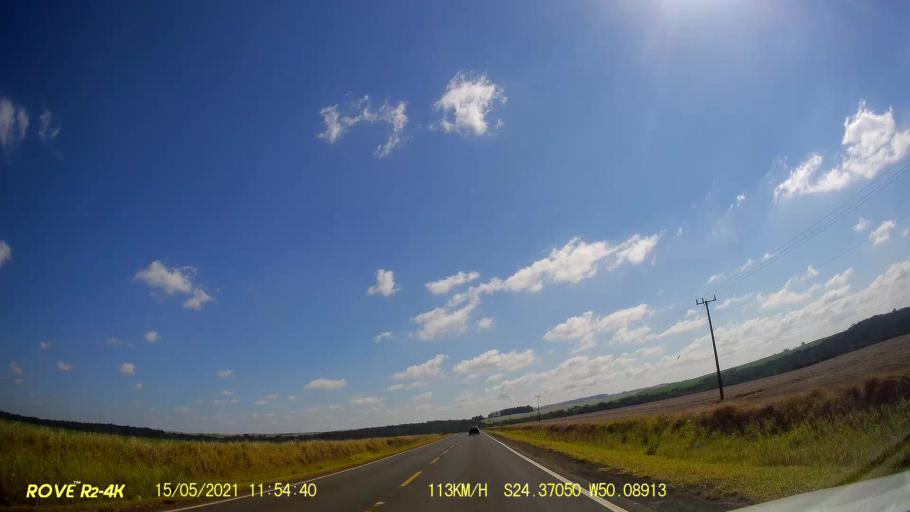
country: BR
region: Parana
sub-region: Pirai Do Sul
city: Pirai do Sul
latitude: -24.3704
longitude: -50.0894
